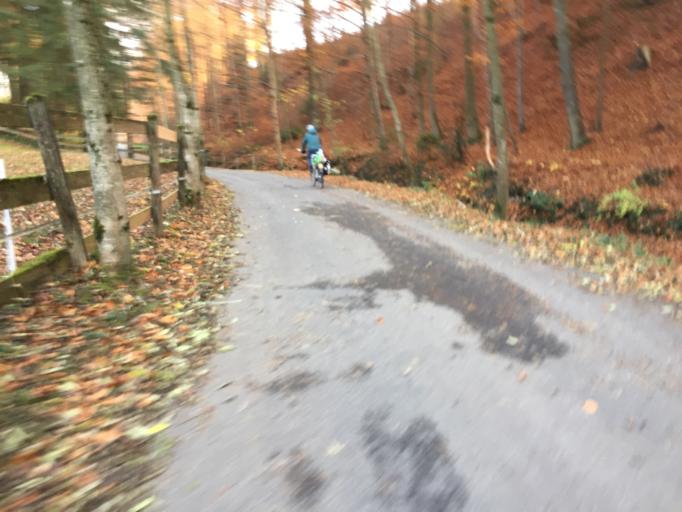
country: CH
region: Bern
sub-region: Bern-Mittelland District
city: Taegertschi
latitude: 46.8774
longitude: 7.5747
